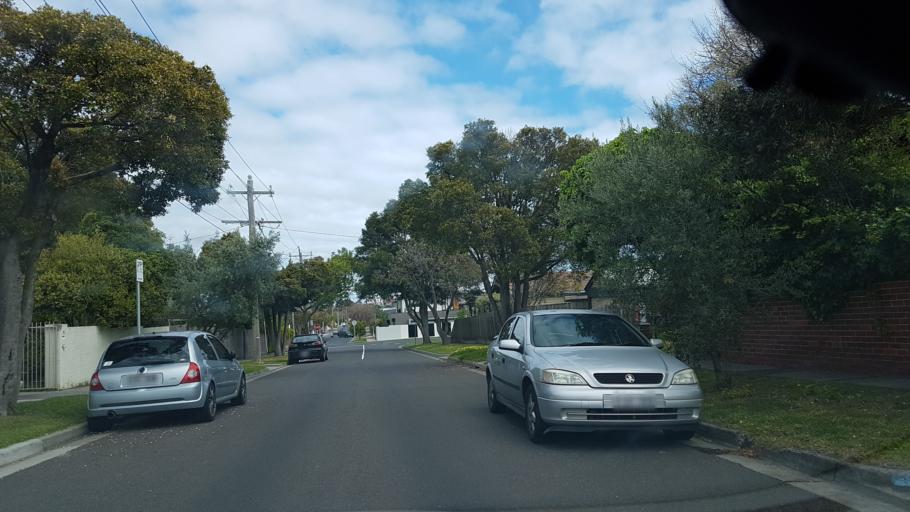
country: AU
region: Victoria
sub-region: Glen Eira
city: Bentleigh
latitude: -37.9216
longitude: 145.0389
